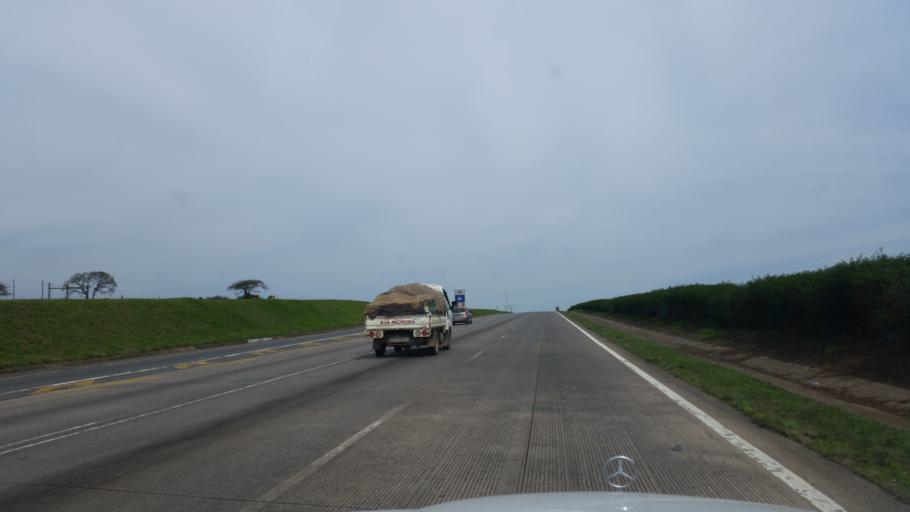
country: ZA
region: KwaZulu-Natal
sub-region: uMgungundlovu District Municipality
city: Camperdown
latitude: -29.6882
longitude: 30.4793
